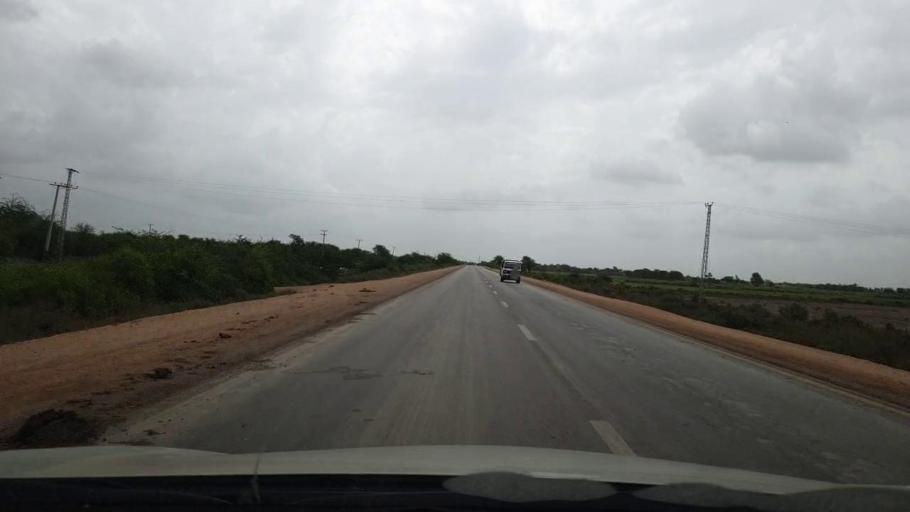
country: PK
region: Sindh
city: Mirpur Batoro
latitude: 24.6232
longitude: 68.3264
